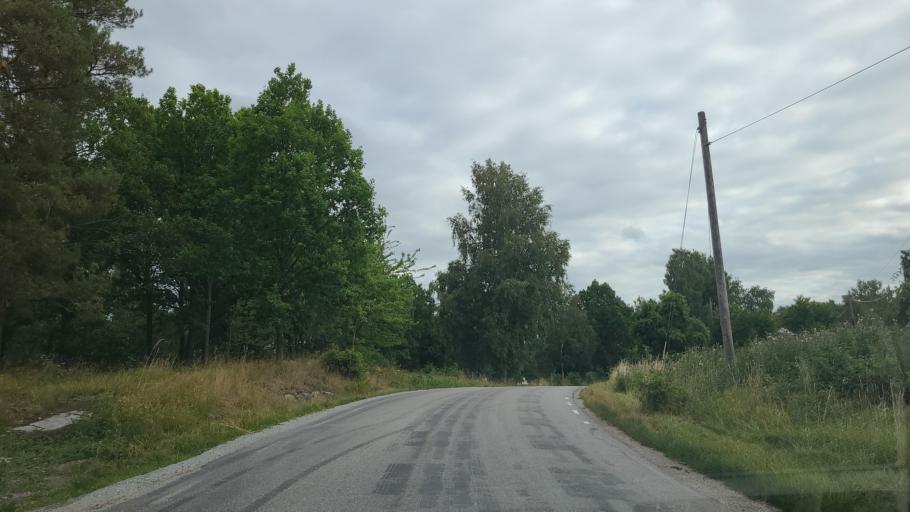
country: SE
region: Stockholm
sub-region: Upplands-Bro Kommun
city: Bro
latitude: 59.4875
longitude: 17.6038
